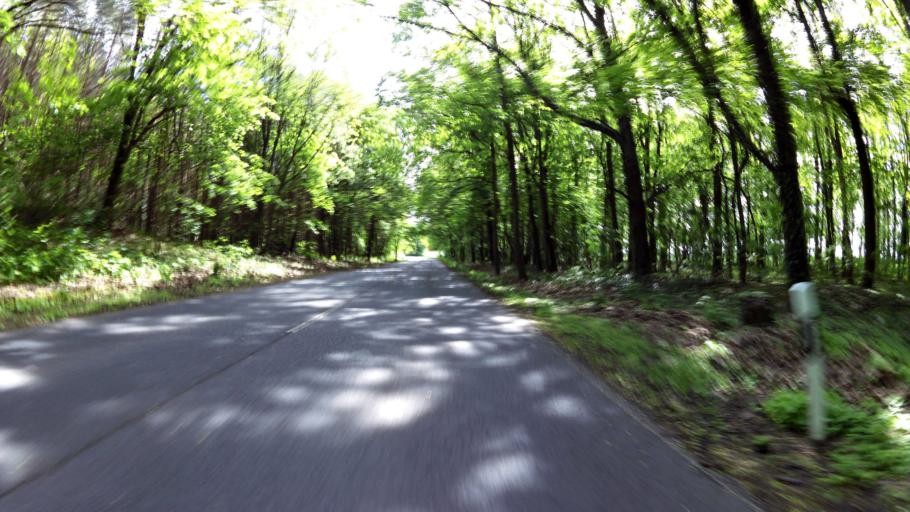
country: DE
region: Brandenburg
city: Glienicke
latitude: 52.6619
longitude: 13.3209
